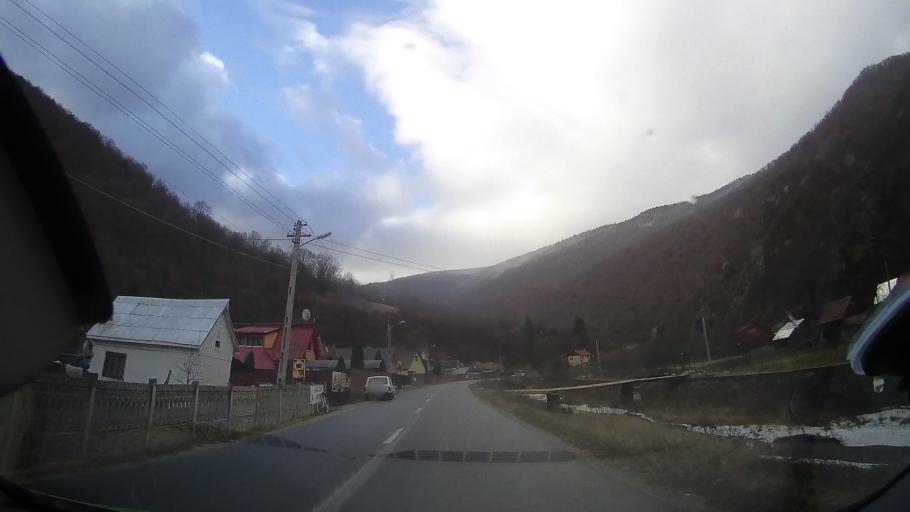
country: RO
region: Cluj
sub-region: Comuna Valea Ierii
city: Valea Ierii
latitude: 46.6851
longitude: 23.2806
